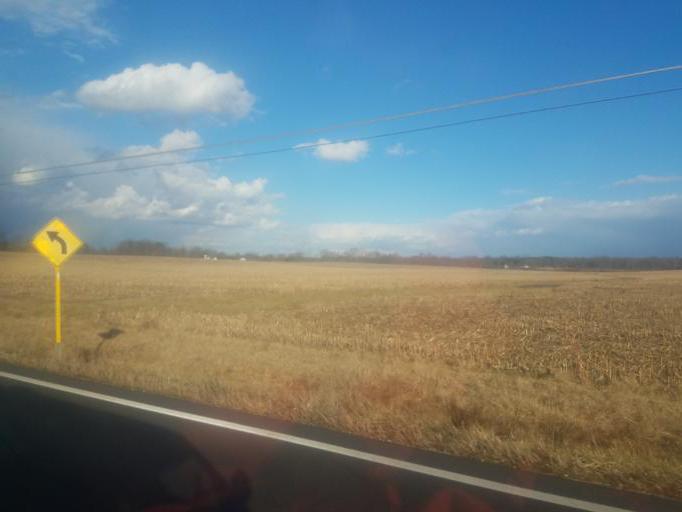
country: US
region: Ohio
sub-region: Delaware County
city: Delaware
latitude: 40.3439
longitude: -83.1362
